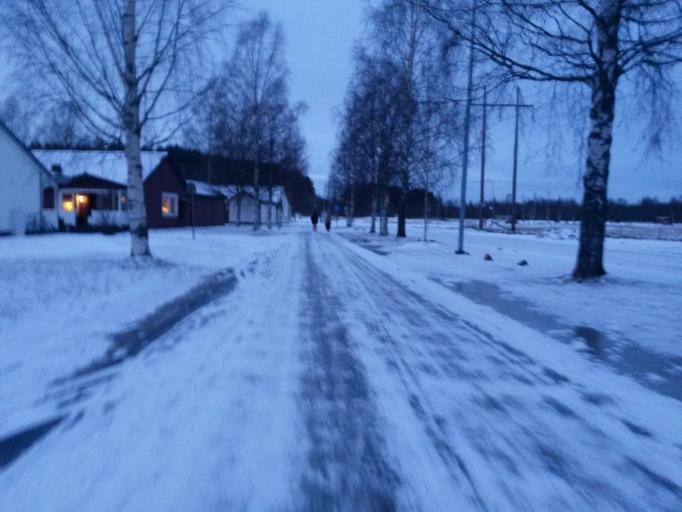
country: SE
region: Vaesterbotten
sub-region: Umea Kommun
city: Umea
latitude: 63.8413
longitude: 20.2176
